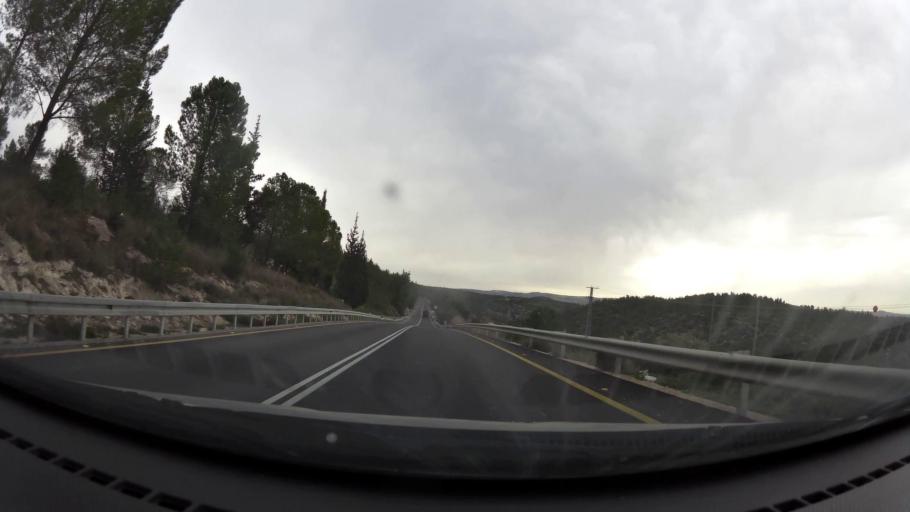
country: PS
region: West Bank
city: Surif
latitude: 31.6736
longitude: 35.0205
